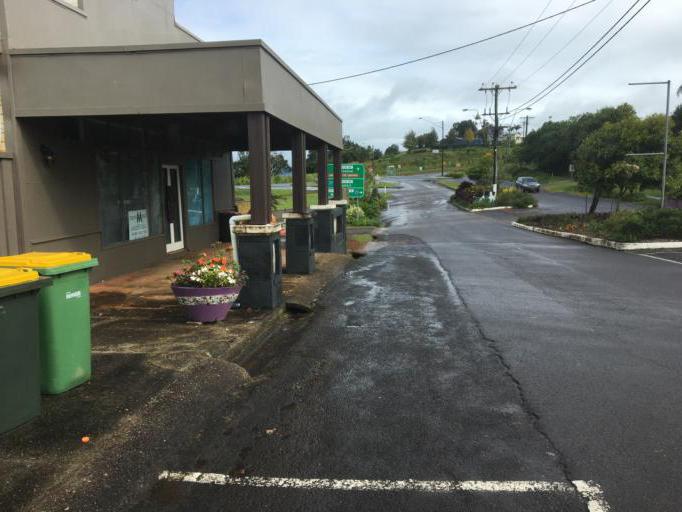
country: AU
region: Queensland
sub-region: Tablelands
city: Ravenshoe
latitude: -17.5122
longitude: 145.6135
